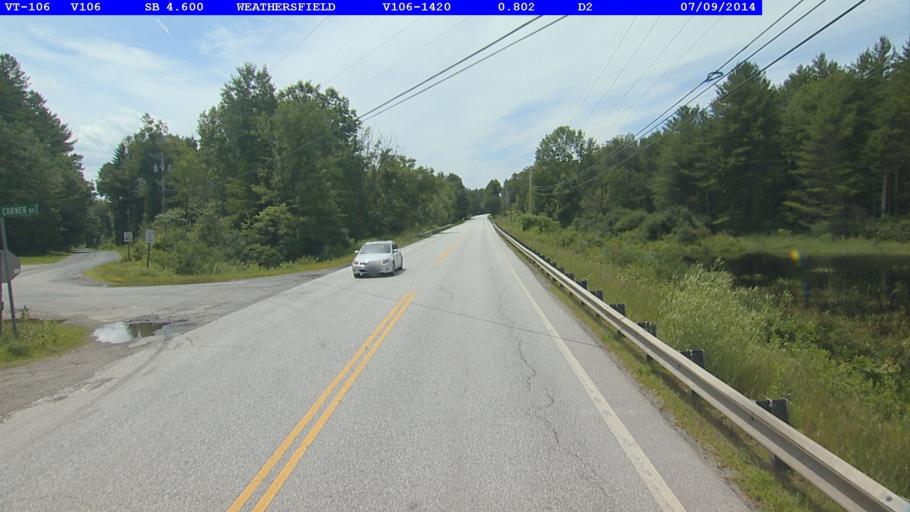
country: US
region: Vermont
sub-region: Windsor County
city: Springfield
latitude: 43.3544
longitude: -72.5232
